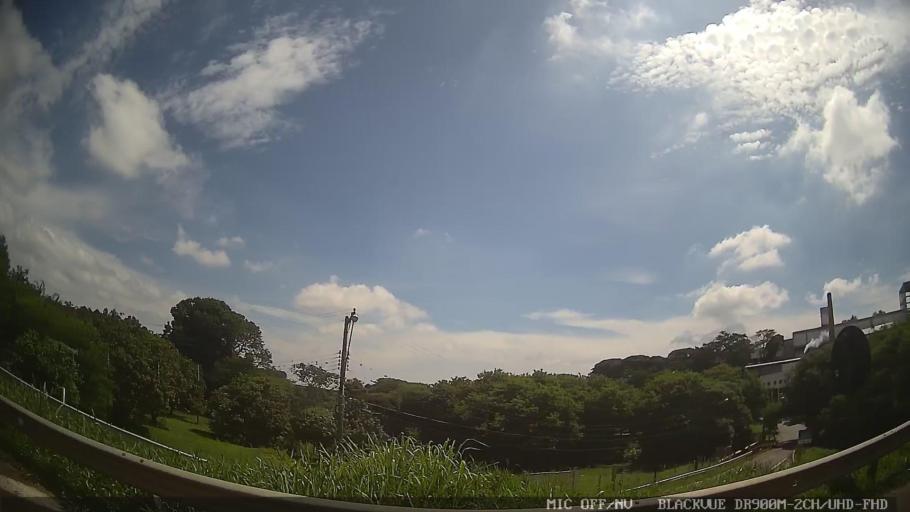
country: BR
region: Sao Paulo
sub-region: Tiete
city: Tiete
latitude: -23.1178
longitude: -47.7235
